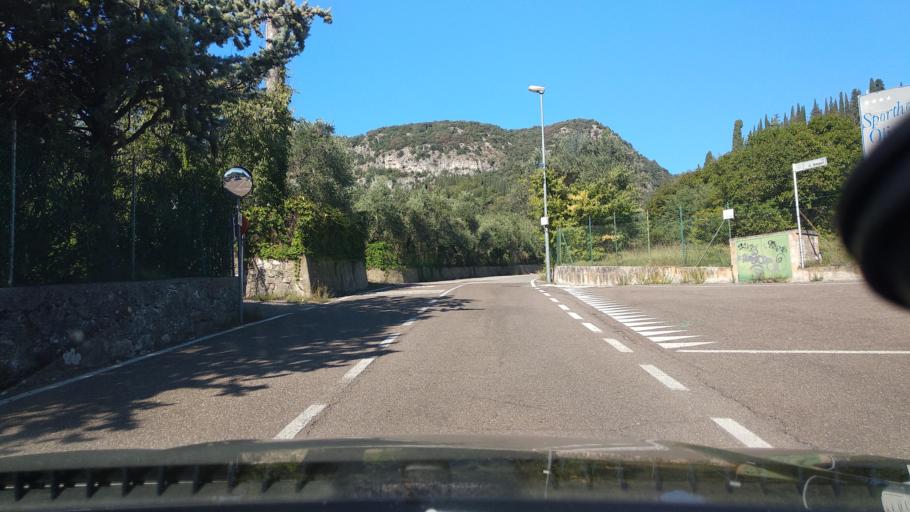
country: IT
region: Veneto
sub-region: Provincia di Verona
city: Garda
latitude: 45.5806
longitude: 10.7035
